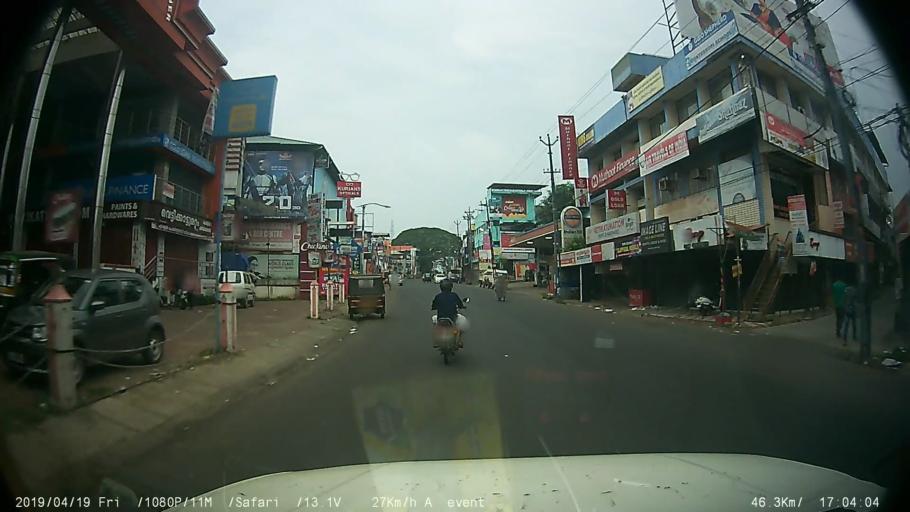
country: IN
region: Kerala
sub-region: Kottayam
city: Changanacheri
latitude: 9.4473
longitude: 76.5421
